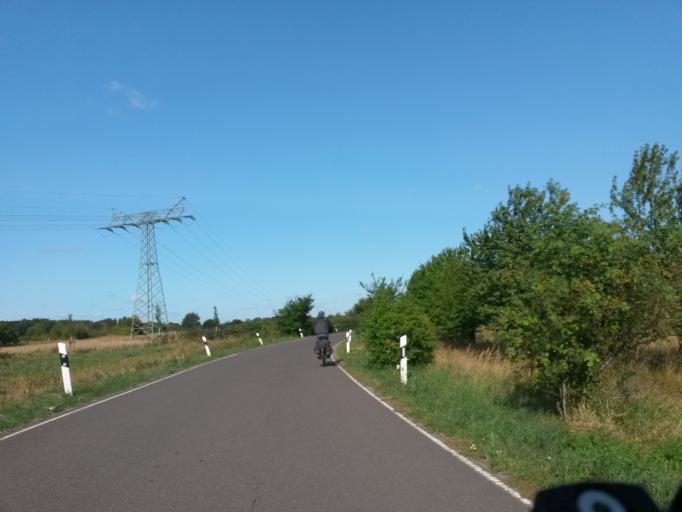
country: DE
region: Saxony-Anhalt
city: Tangermunde
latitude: 52.5719
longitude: 11.9654
